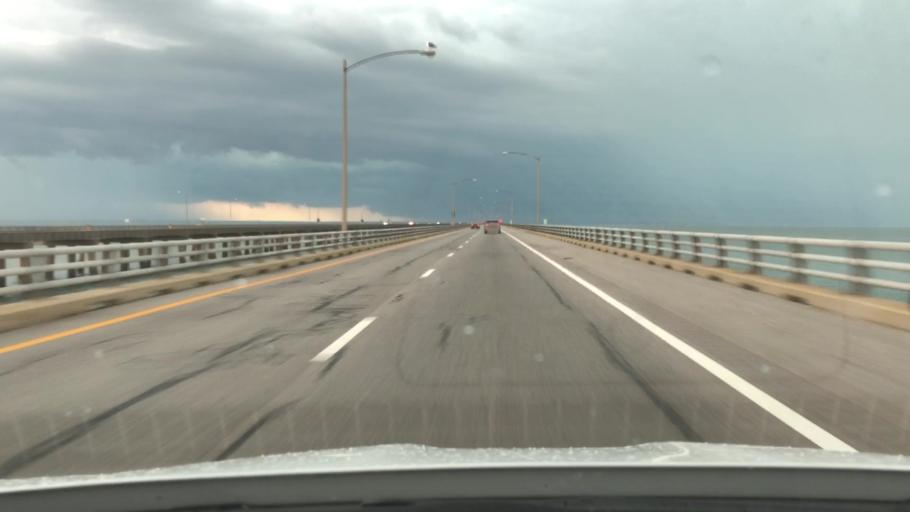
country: US
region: Virginia
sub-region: City of Virginia Beach
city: Virginia Beach
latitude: 37.0240
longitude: -76.0899
